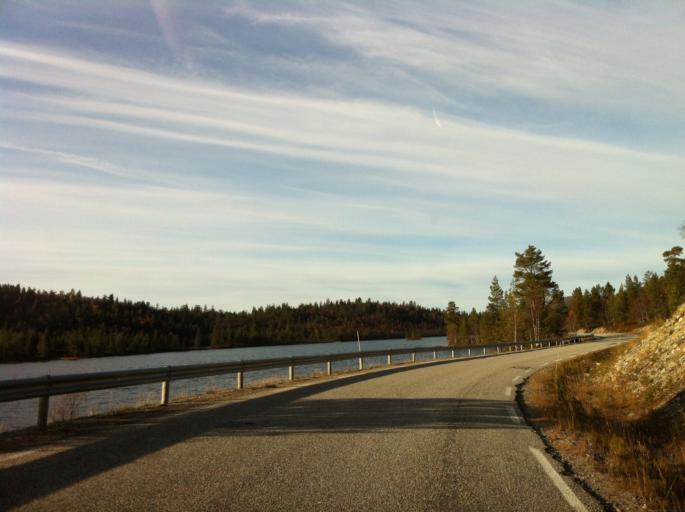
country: NO
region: Hedmark
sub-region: Engerdal
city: Engerdal
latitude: 62.0970
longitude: 12.0327
